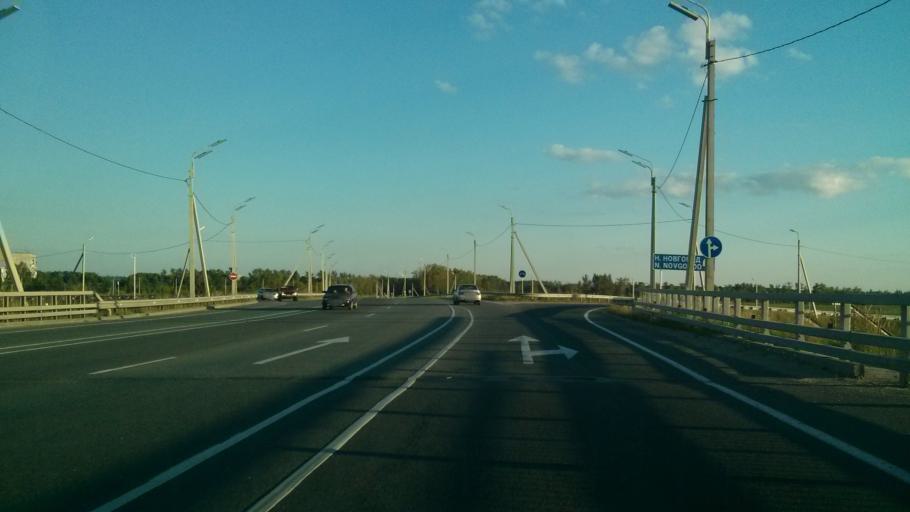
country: RU
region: Vladimir
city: Murom
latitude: 55.6185
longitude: 42.0244
